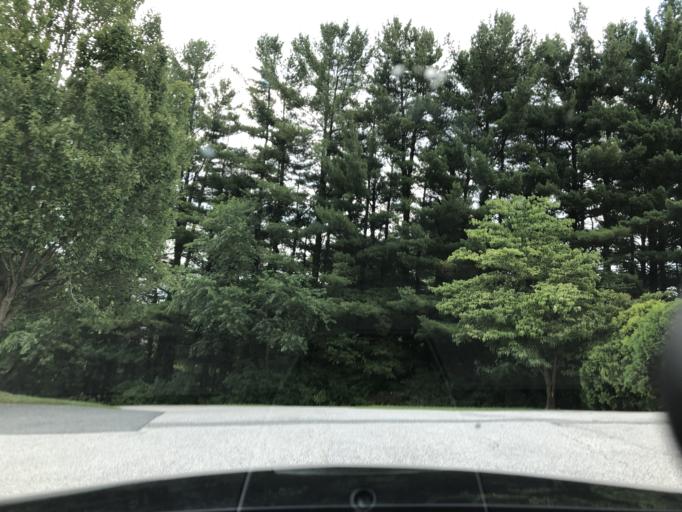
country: US
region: Maryland
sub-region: Carroll County
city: Westminster
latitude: 39.5547
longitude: -76.9818
